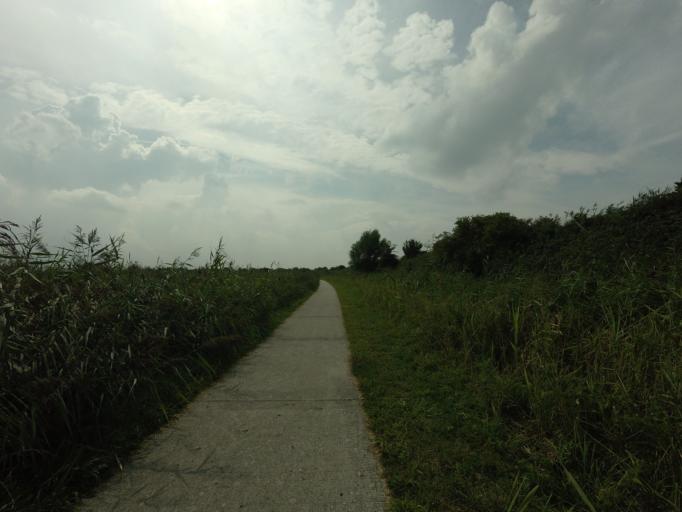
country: NL
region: Flevoland
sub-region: Gemeente Almere
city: Almere Stad
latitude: 52.3996
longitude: 5.1934
